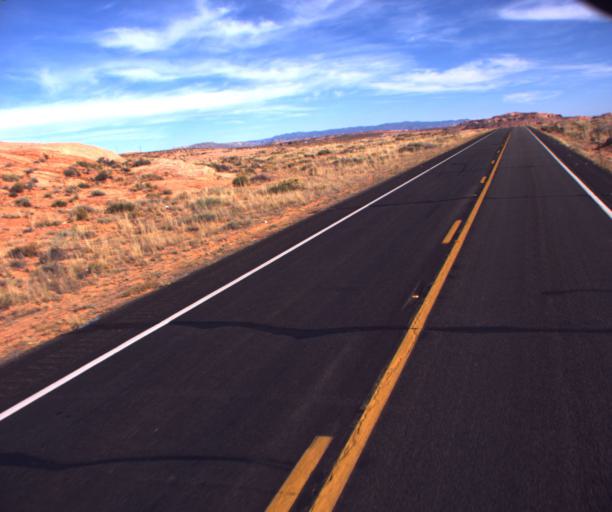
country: US
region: Arizona
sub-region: Apache County
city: Many Farms
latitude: 36.9341
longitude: -109.6308
